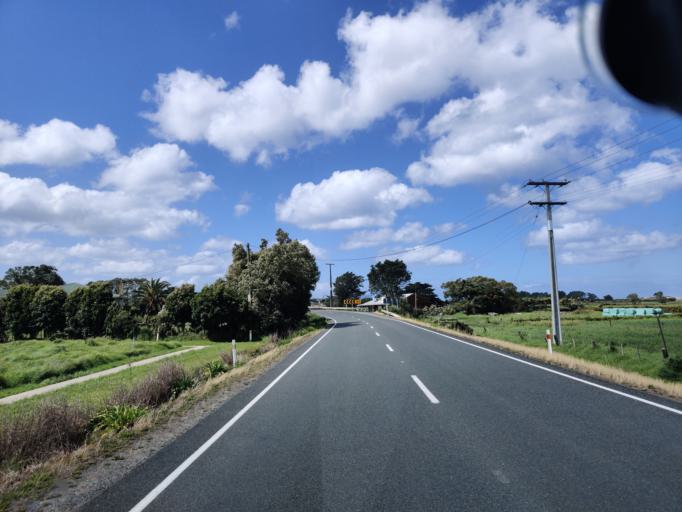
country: NZ
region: Northland
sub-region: Whangarei
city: Ruakaka
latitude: -35.9784
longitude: 174.4529
